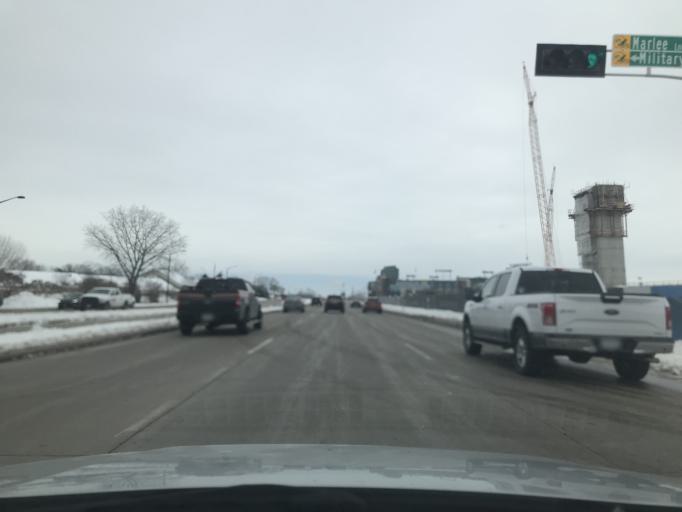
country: US
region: Wisconsin
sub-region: Brown County
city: Ashwaubenon
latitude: 44.5064
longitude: -88.0713
